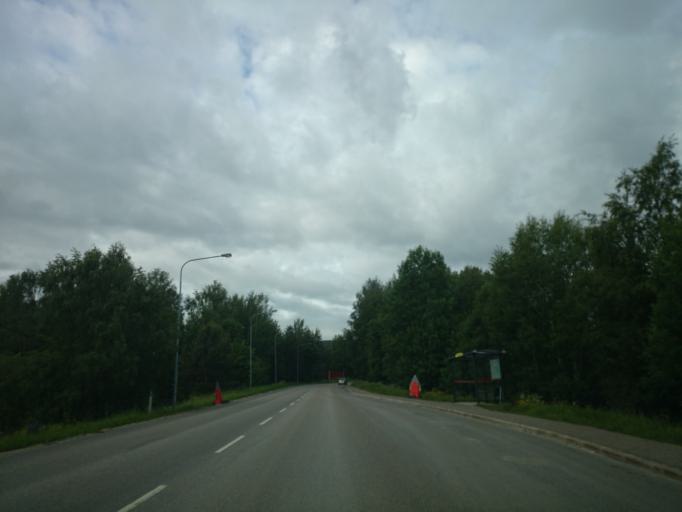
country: SE
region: Vaesternorrland
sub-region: Sundsvalls Kommun
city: Stockvik
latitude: 62.3748
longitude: 17.3598
